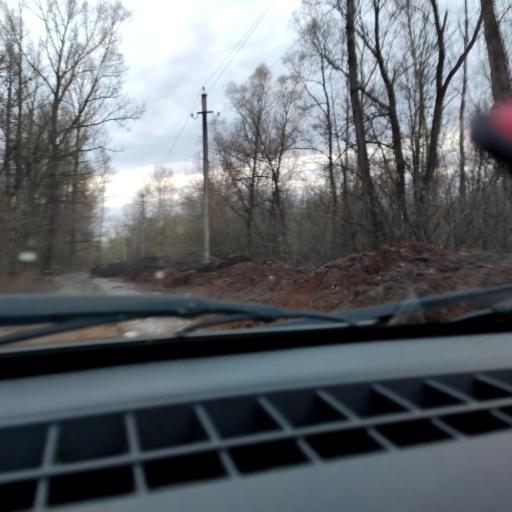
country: RU
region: Bashkortostan
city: Ufa
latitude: 54.6794
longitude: 55.9514
